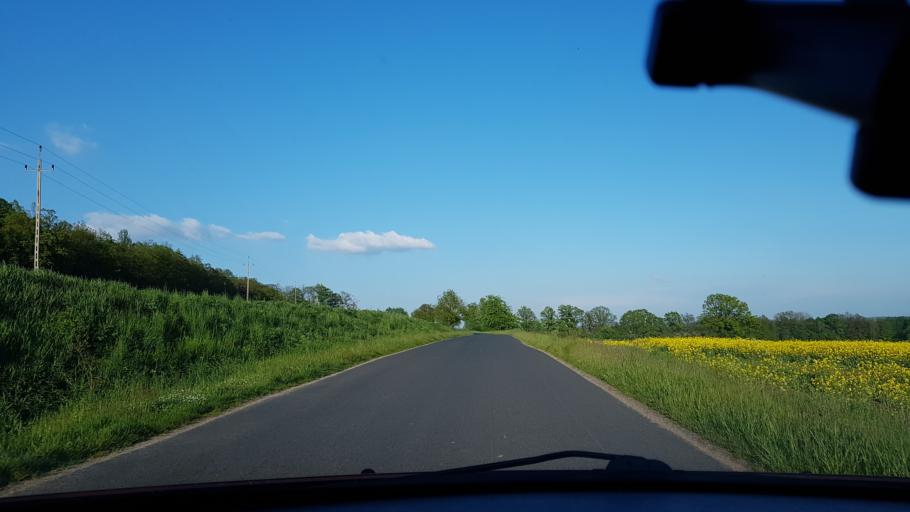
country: PL
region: Lower Silesian Voivodeship
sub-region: Powiat zabkowicki
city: Budzow
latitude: 50.6130
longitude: 16.6838
